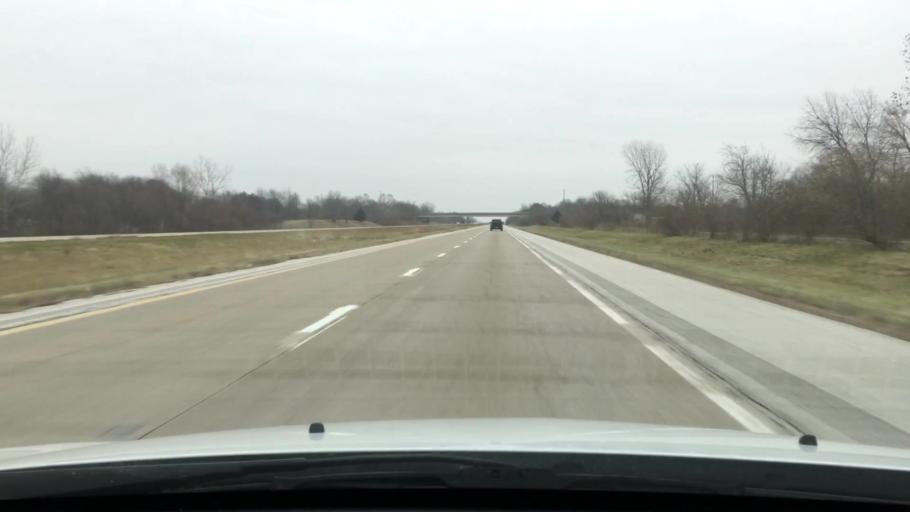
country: US
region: Illinois
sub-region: Scott County
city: Winchester
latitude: 39.6810
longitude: -90.5100
